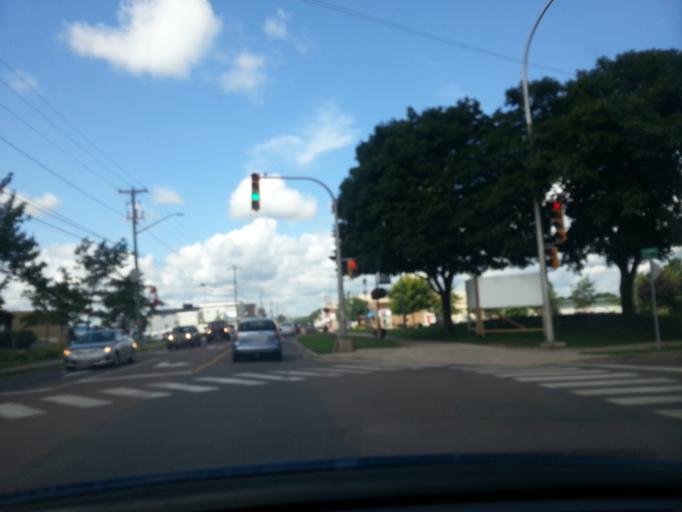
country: CA
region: New Brunswick
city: Shediac
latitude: 46.2195
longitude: -64.5405
